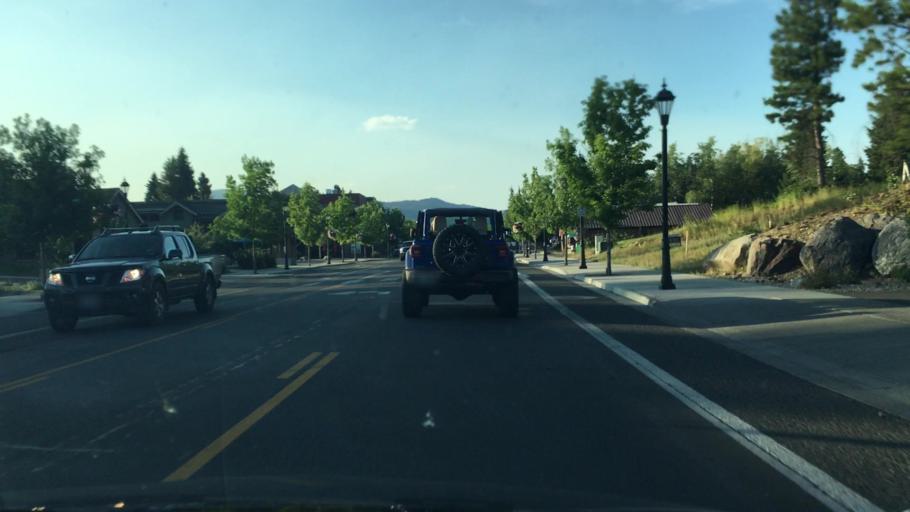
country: US
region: Idaho
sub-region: Valley County
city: McCall
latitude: 44.9065
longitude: -116.0975
